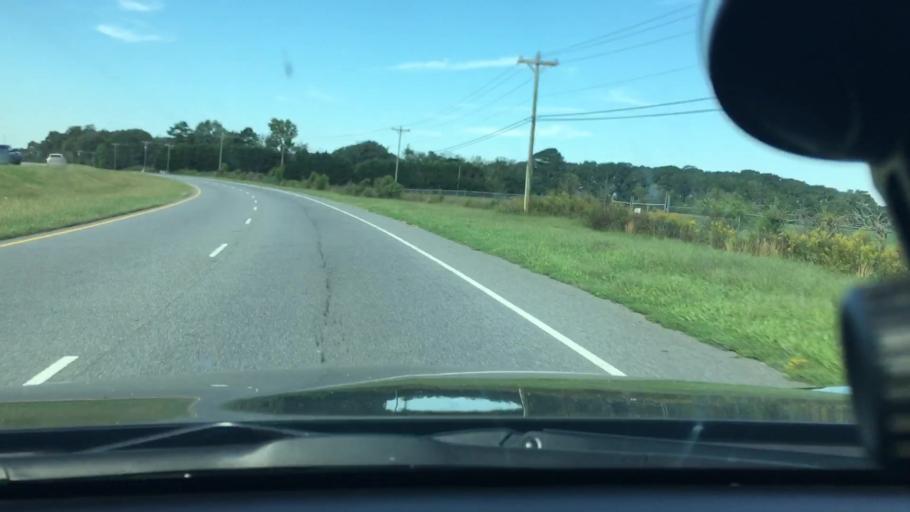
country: US
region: North Carolina
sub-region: Cabarrus County
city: Midland
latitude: 35.2558
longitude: -80.4761
